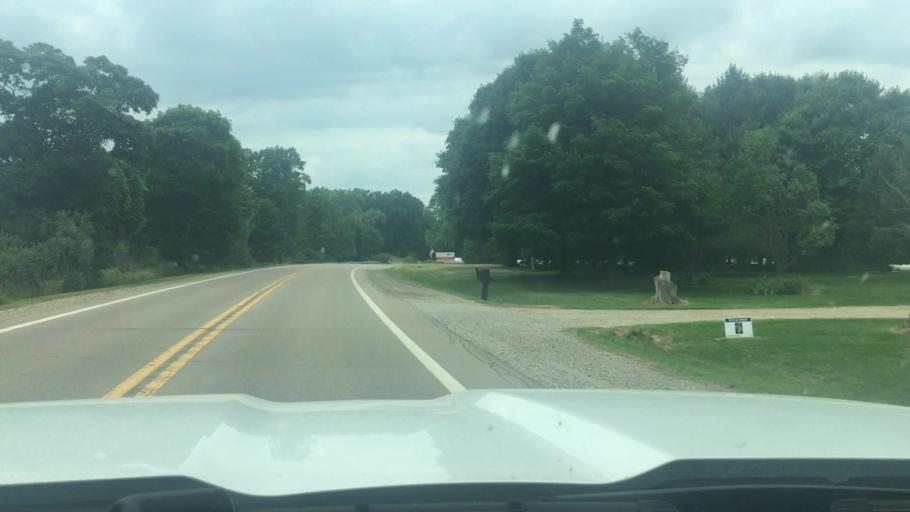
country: US
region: Michigan
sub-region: Clinton County
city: Fowler
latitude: 42.9963
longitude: -84.8650
